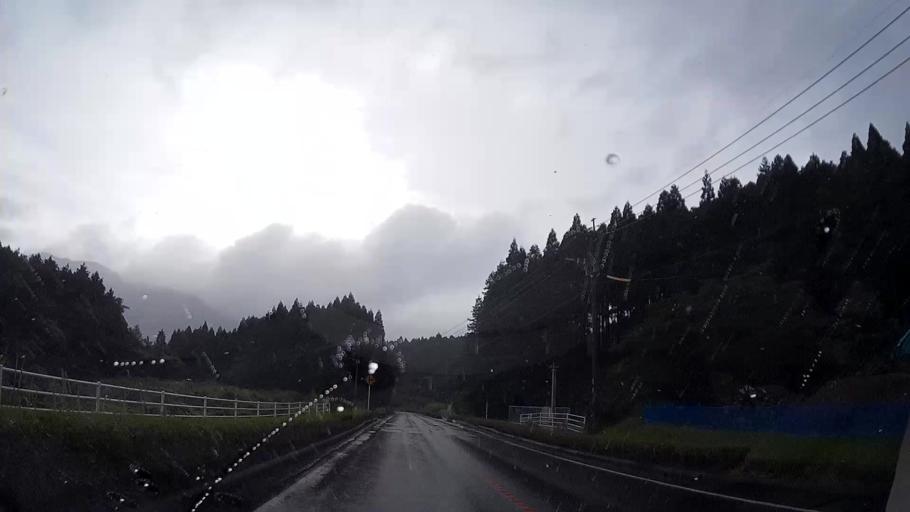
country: JP
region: Kumamoto
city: Aso
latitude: 32.8560
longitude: 131.0157
